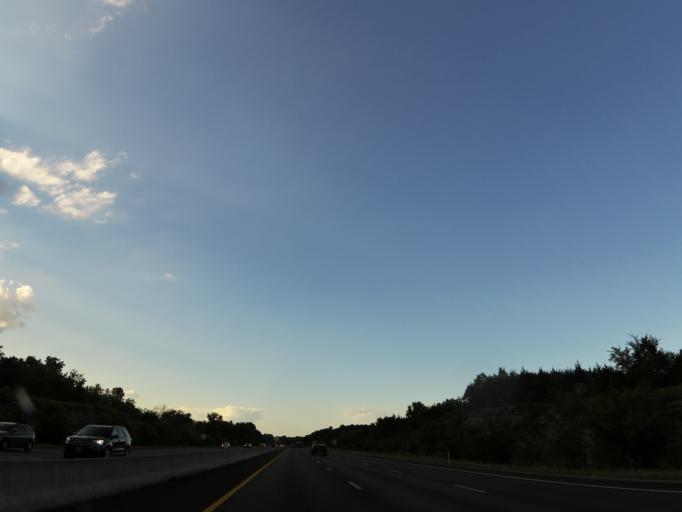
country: US
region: Tennessee
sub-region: Maury County
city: Spring Hill
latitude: 35.7536
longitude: -86.8689
